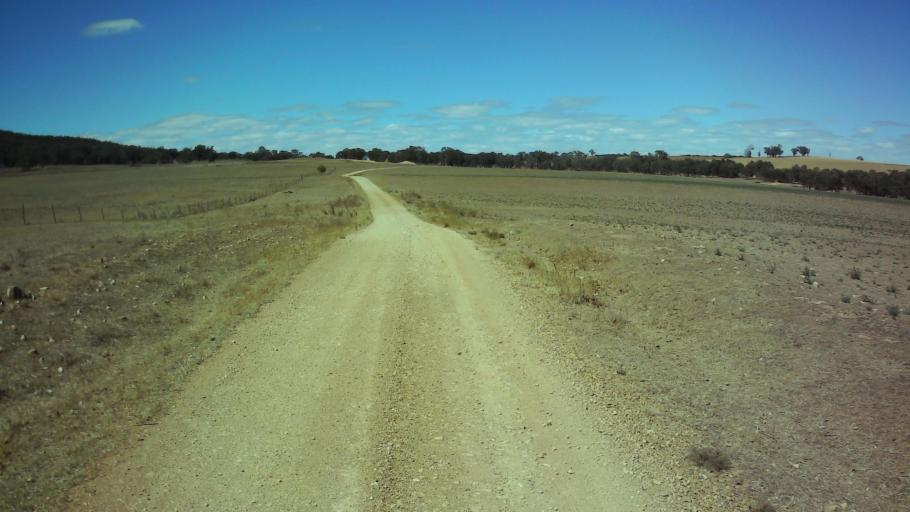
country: AU
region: New South Wales
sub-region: Weddin
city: Grenfell
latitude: -34.0385
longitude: 148.4323
